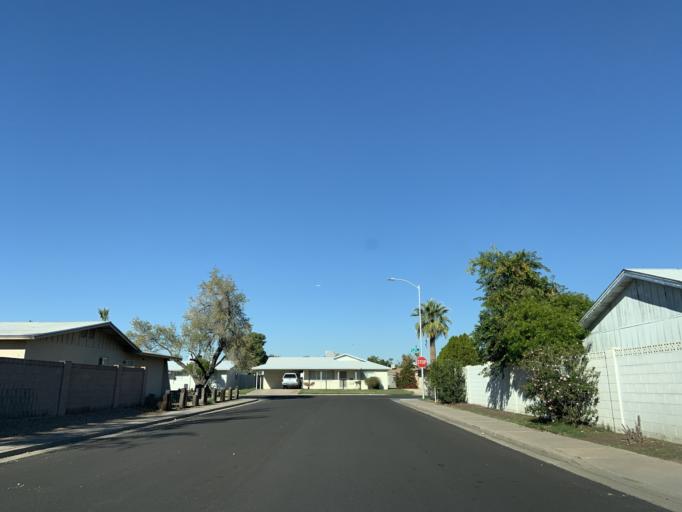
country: US
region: Arizona
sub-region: Maricopa County
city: Tempe
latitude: 33.4014
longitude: -111.8809
